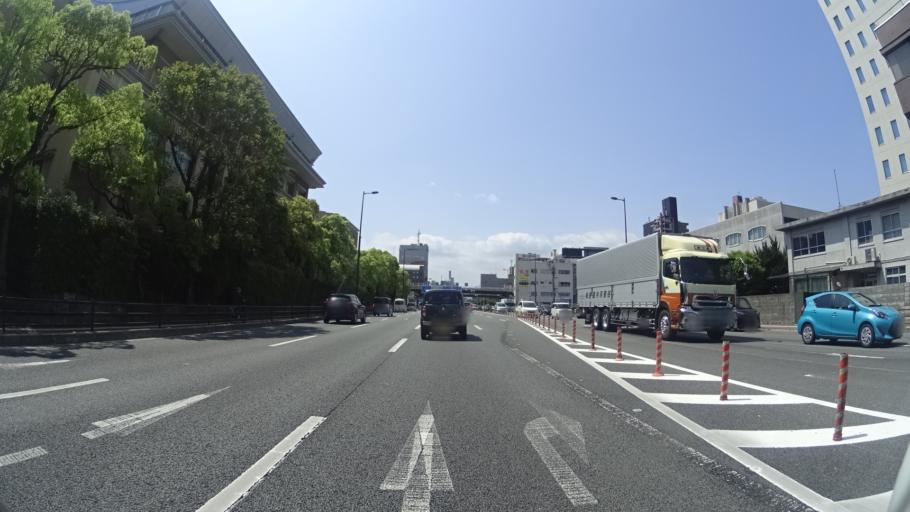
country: JP
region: Tokushima
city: Tokushima-shi
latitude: 34.0730
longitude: 134.5583
